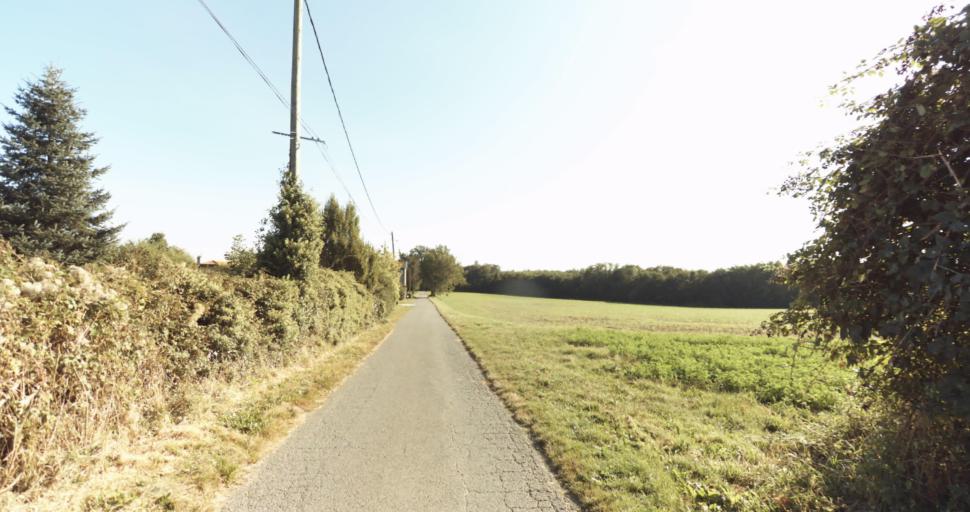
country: FR
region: Rhone-Alpes
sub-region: Departement du Rhone
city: Montanay
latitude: 45.8945
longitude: 4.8565
